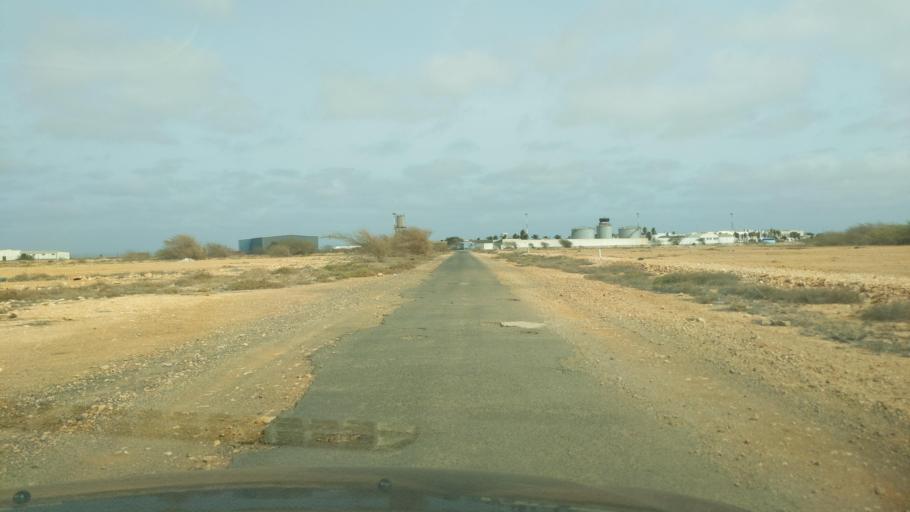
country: CV
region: Sal
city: Espargos
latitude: 16.7296
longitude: -22.9392
